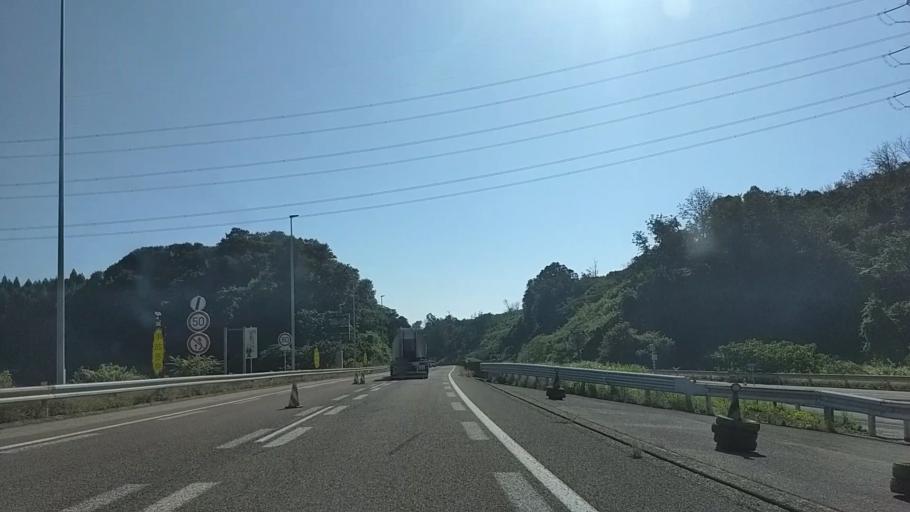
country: JP
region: Toyama
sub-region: Oyabe Shi
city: Oyabe
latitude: 36.6044
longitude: 136.7933
